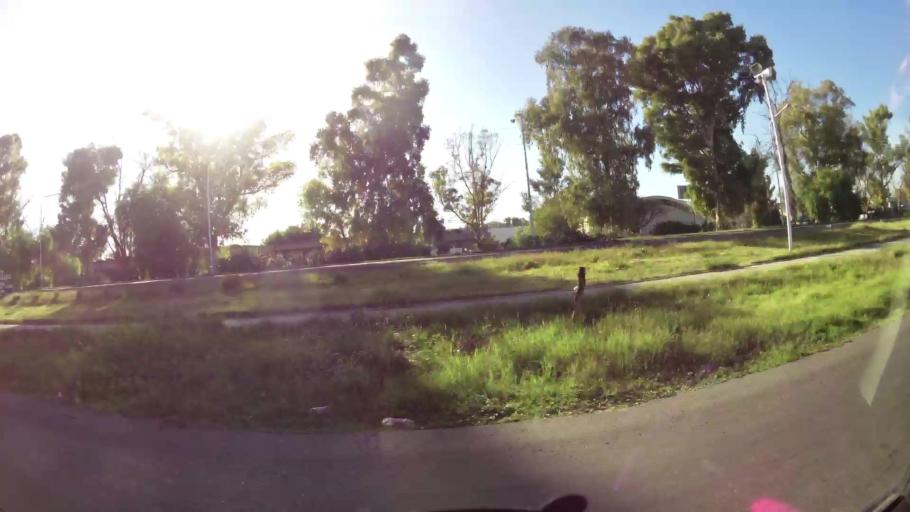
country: AR
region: Mendoza
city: Las Heras
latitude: -32.8593
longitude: -68.8084
